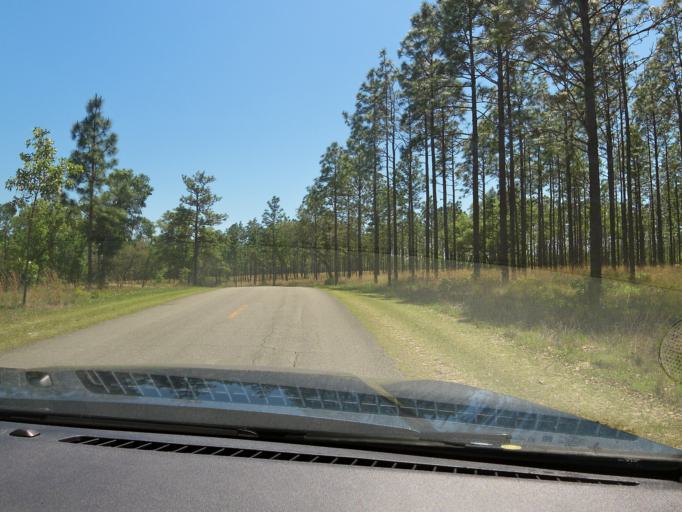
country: US
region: Florida
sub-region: Clay County
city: Keystone Heights
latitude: 29.8275
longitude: -81.9562
